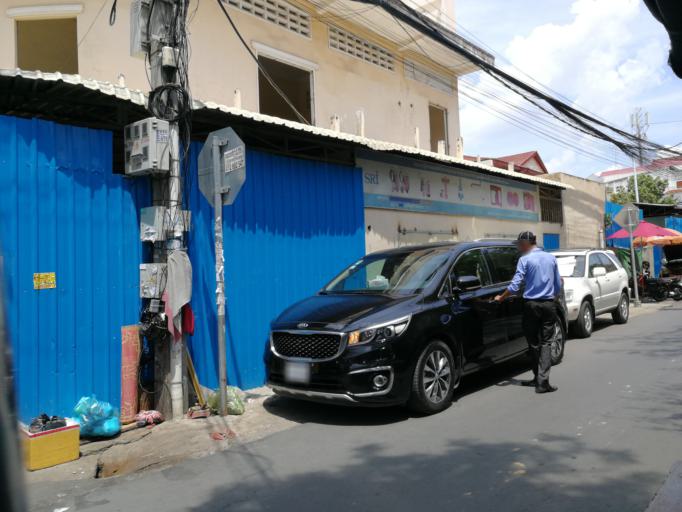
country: KH
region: Phnom Penh
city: Phnom Penh
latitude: 11.5479
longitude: 104.9179
